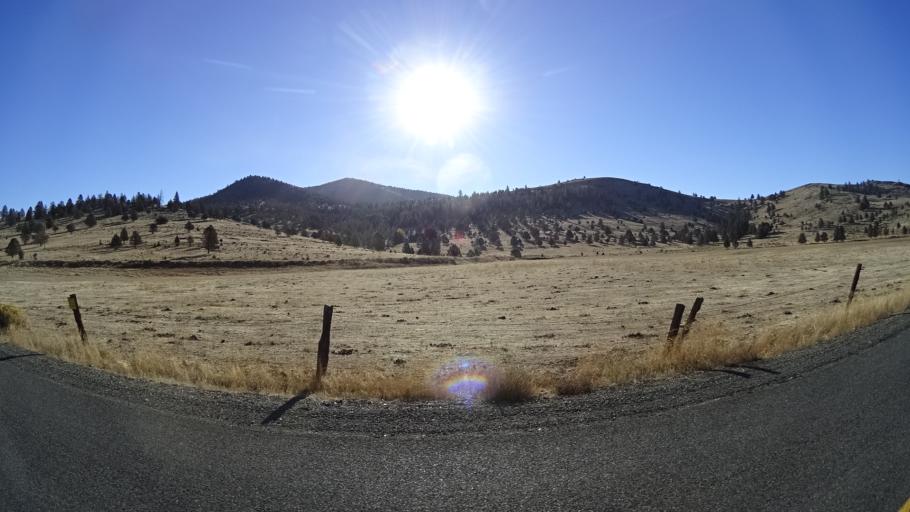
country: US
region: California
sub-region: Siskiyou County
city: Yreka
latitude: 41.4614
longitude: -122.8404
